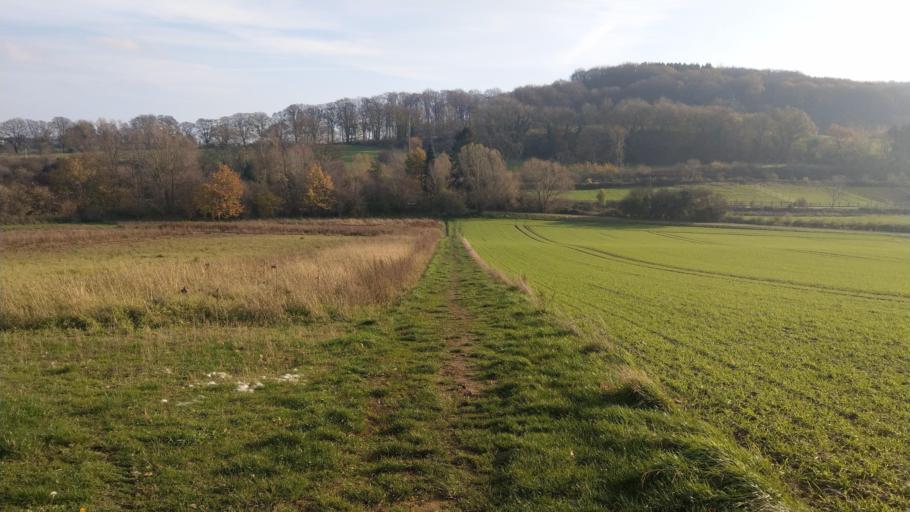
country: NL
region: Limburg
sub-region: Gemeente Vaals
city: Vaals
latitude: 50.7631
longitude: 6.0368
